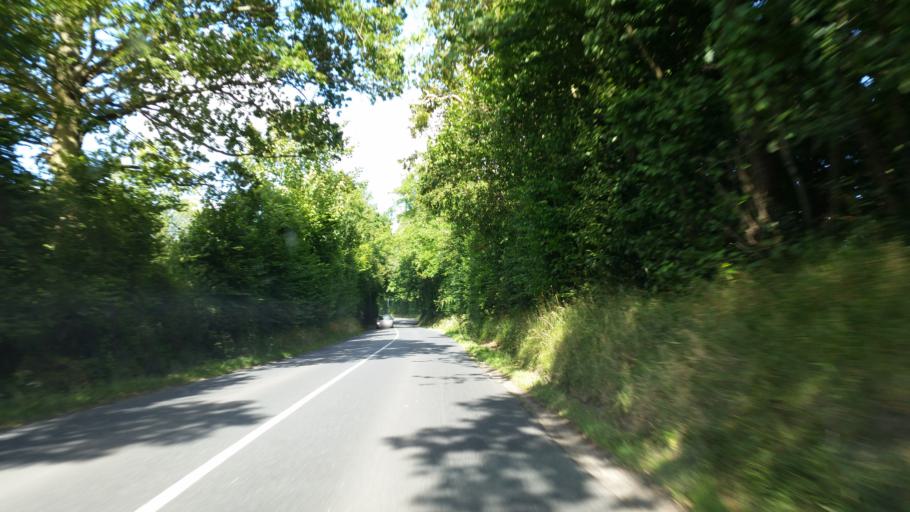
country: FR
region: Lower Normandy
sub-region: Departement du Calvados
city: Dozule
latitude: 49.2574
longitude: -0.0544
